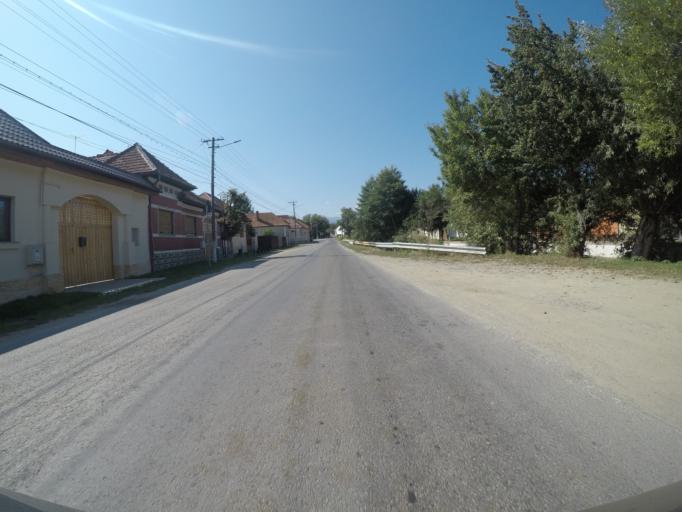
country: RO
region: Brasov
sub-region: Comuna Sinca Veche
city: Sinca Veche
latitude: 45.7472
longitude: 25.1240
